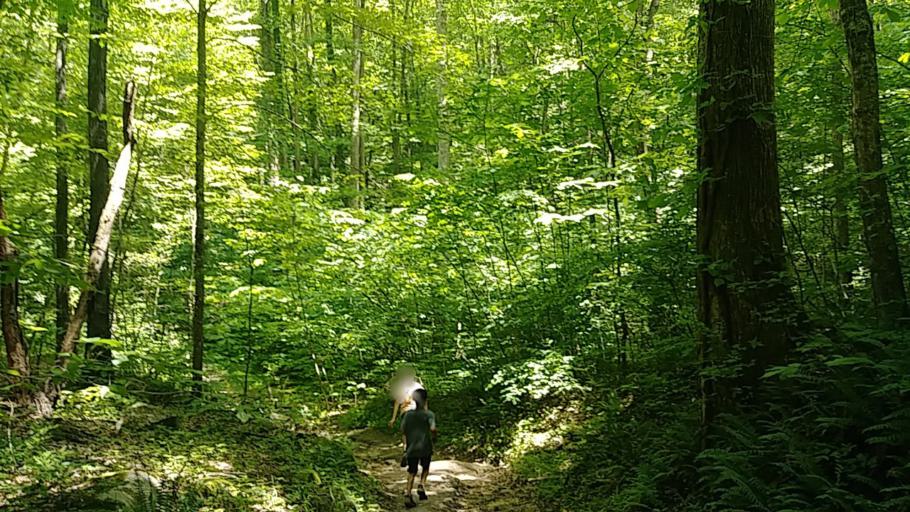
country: US
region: Tennessee
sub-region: Claiborne County
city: Harrogate
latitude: 36.6031
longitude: -83.6770
